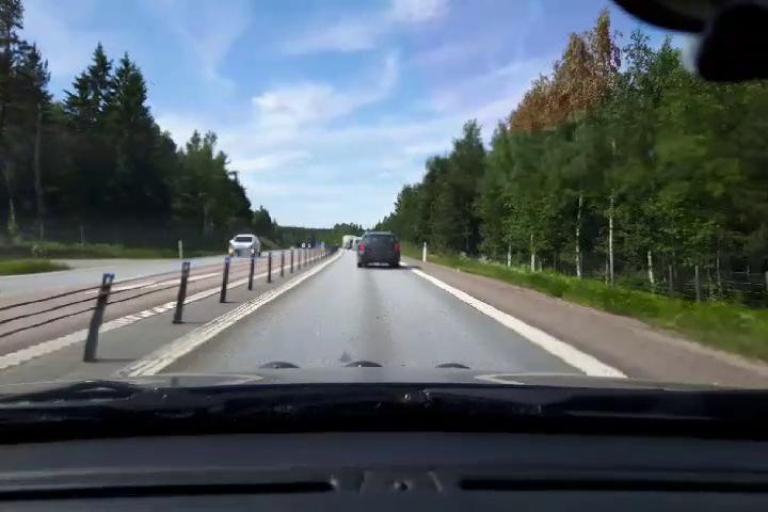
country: SE
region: Gaevleborg
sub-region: Gavle Kommun
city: Norrsundet
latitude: 60.8956
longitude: 17.0293
